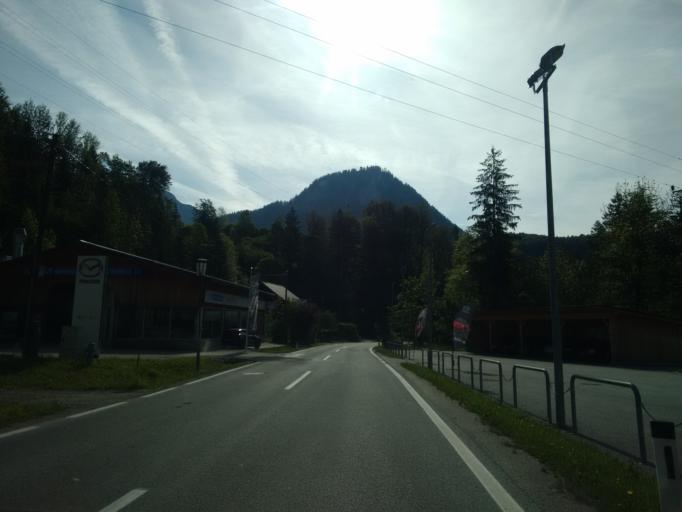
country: AT
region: Styria
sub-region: Politischer Bezirk Liezen
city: Altaussee
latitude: 47.6278
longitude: 13.7664
